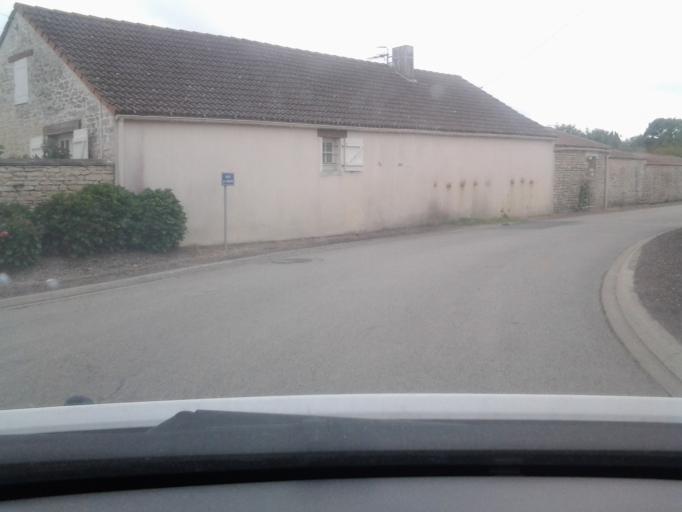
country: FR
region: Pays de la Loire
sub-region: Departement de la Vendee
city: Angles
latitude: 46.3936
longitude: -1.4110
